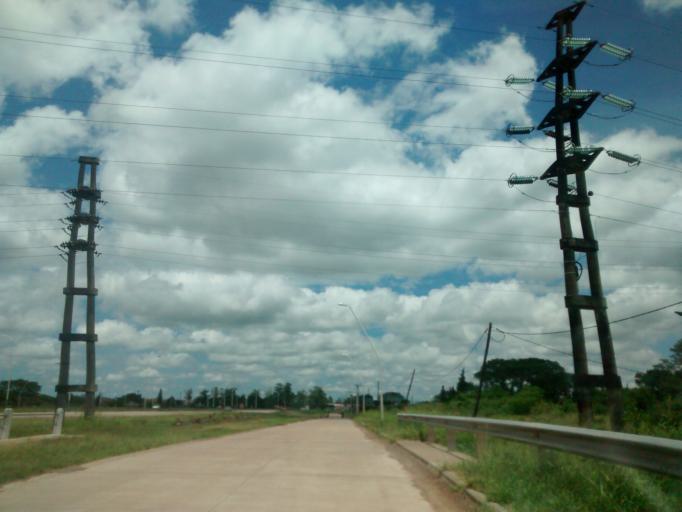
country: AR
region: Chaco
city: Fontana
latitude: -27.4095
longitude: -58.9898
